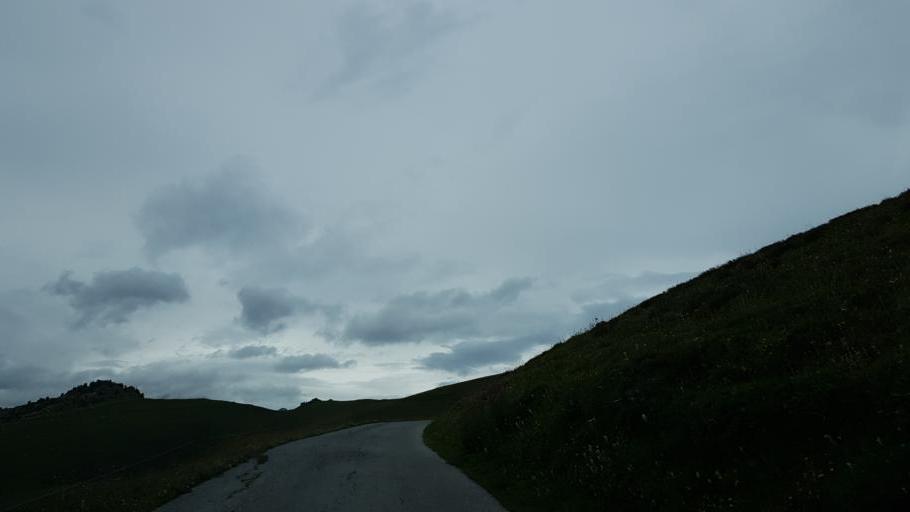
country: IT
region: Piedmont
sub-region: Provincia di Cuneo
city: Serre
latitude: 44.5447
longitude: 7.1182
